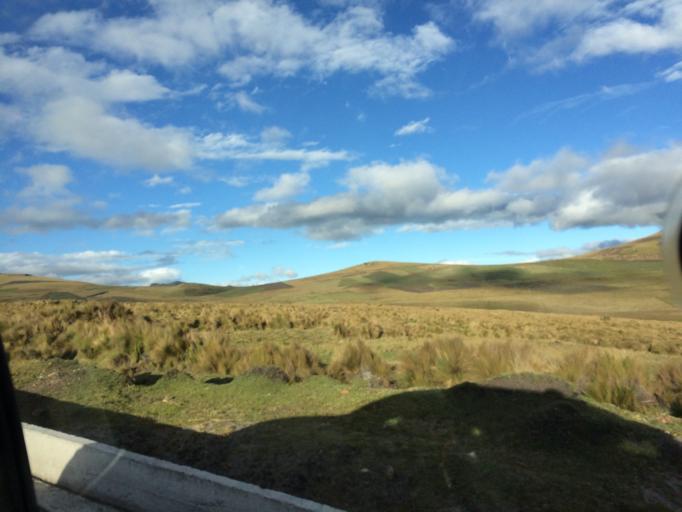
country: EC
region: Chimborazo
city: Alausi
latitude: -2.2347
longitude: -78.6832
